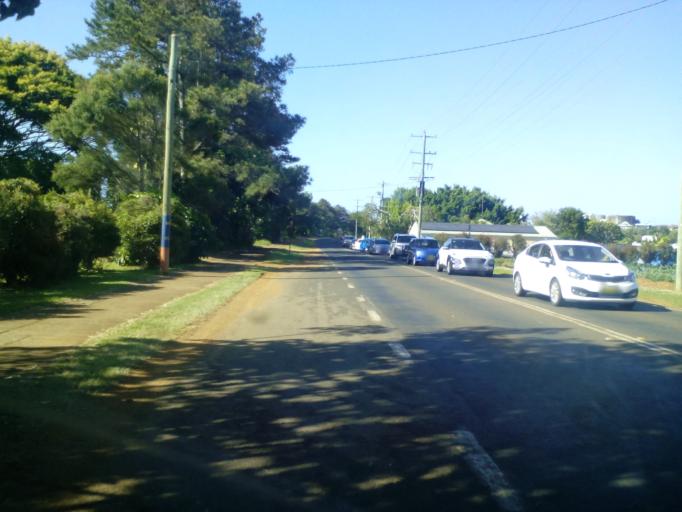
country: AU
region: New South Wales
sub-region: Tweed
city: Kingscliff
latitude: -28.2658
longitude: 153.5663
